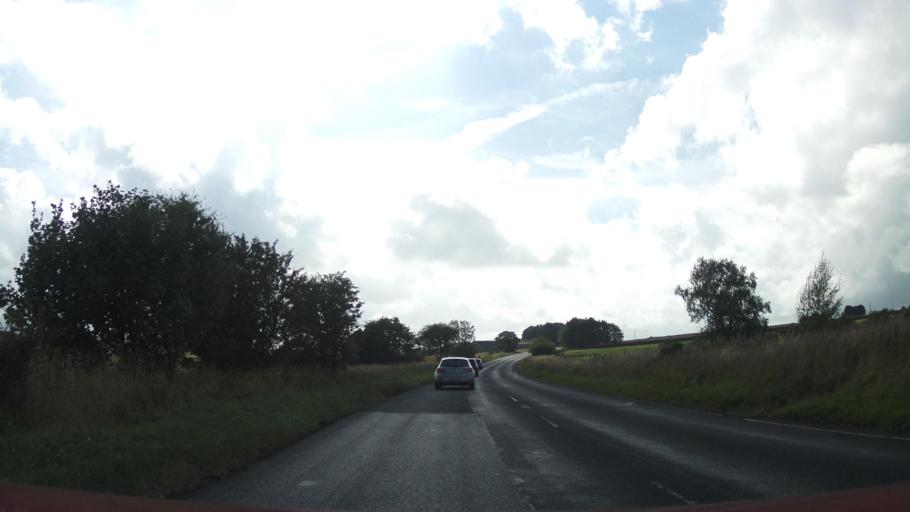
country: GB
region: England
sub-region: Northumberland
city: Healey
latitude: 54.8820
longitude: -1.9402
